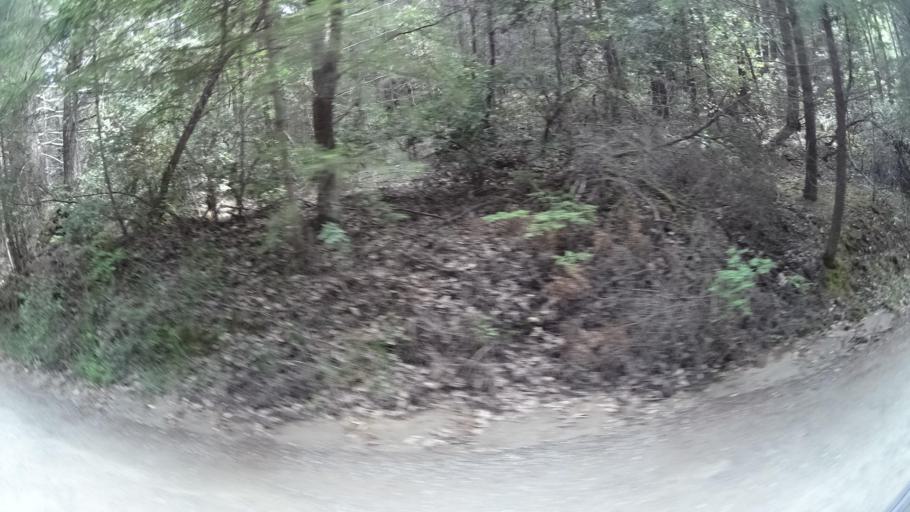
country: US
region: California
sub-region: Humboldt County
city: Redway
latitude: 40.0320
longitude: -123.8363
